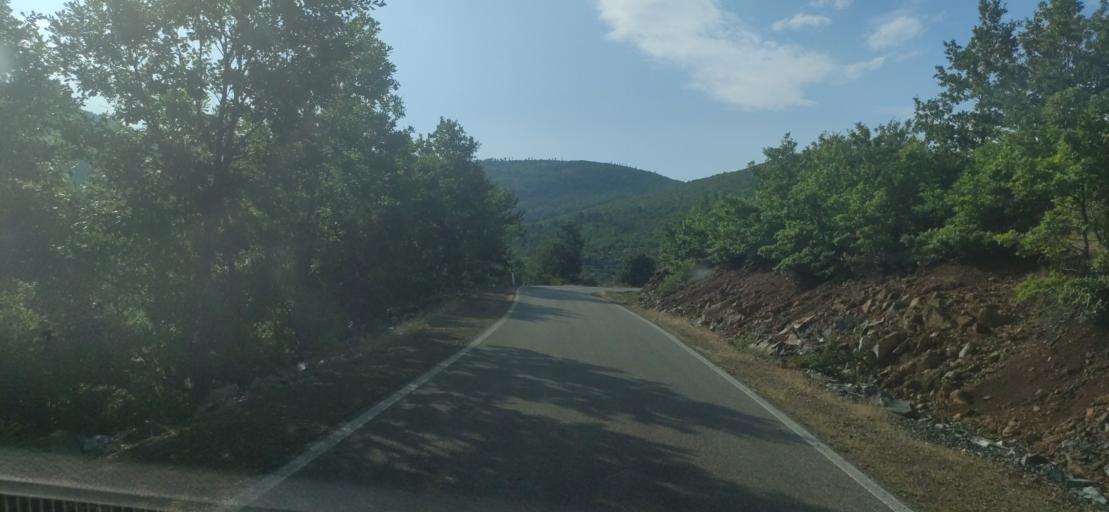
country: AL
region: Shkoder
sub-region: Rrethi i Pukes
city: Iballe
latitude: 42.1808
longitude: 20.0001
